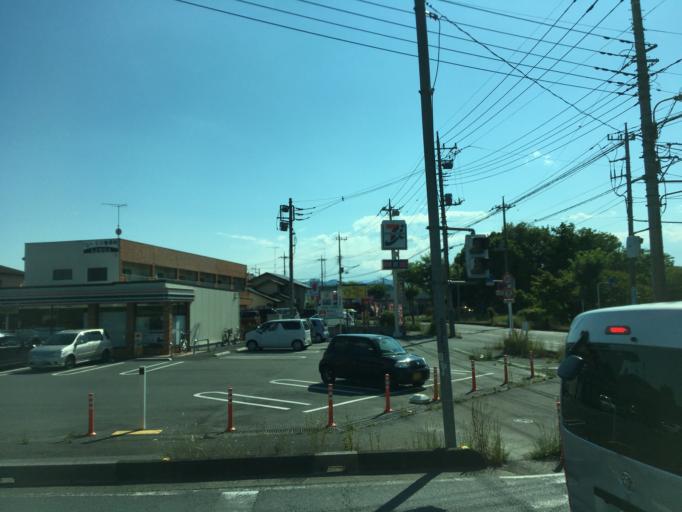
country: JP
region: Saitama
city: Sakado
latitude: 35.9701
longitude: 139.3421
